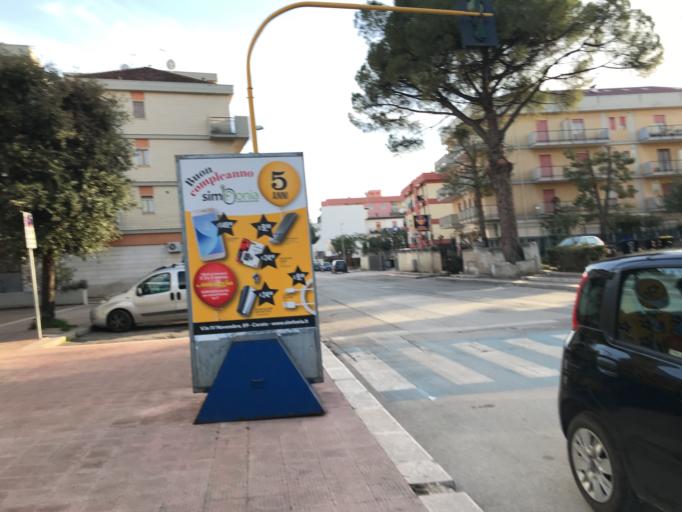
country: IT
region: Apulia
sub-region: Provincia di Bari
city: Corato
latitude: 41.1471
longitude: 16.4097
